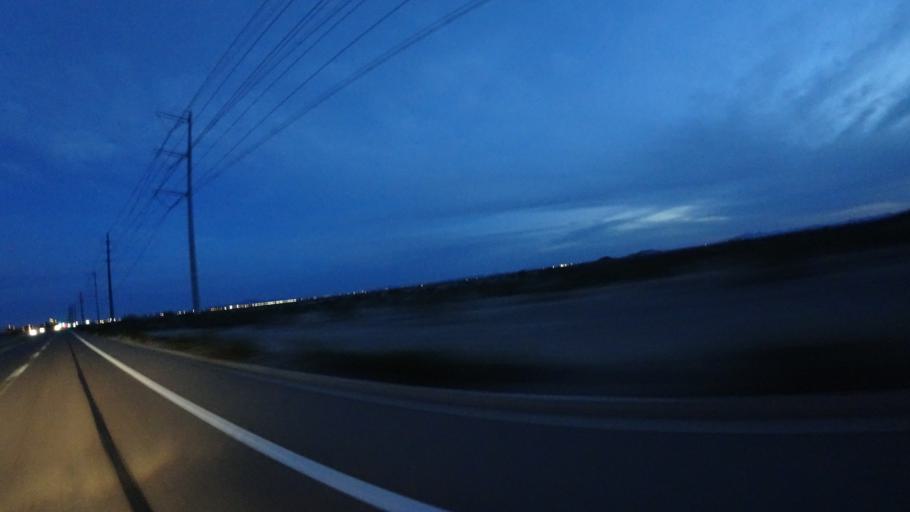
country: US
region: Arizona
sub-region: Maricopa County
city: Guadalupe
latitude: 33.2910
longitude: -112.0400
